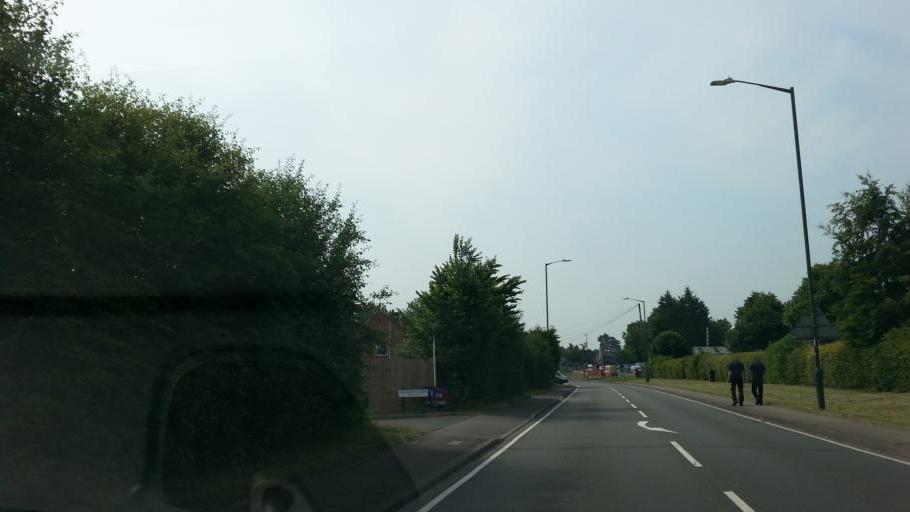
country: GB
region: England
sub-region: Warwickshire
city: Studley
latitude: 52.2772
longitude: -1.8951
